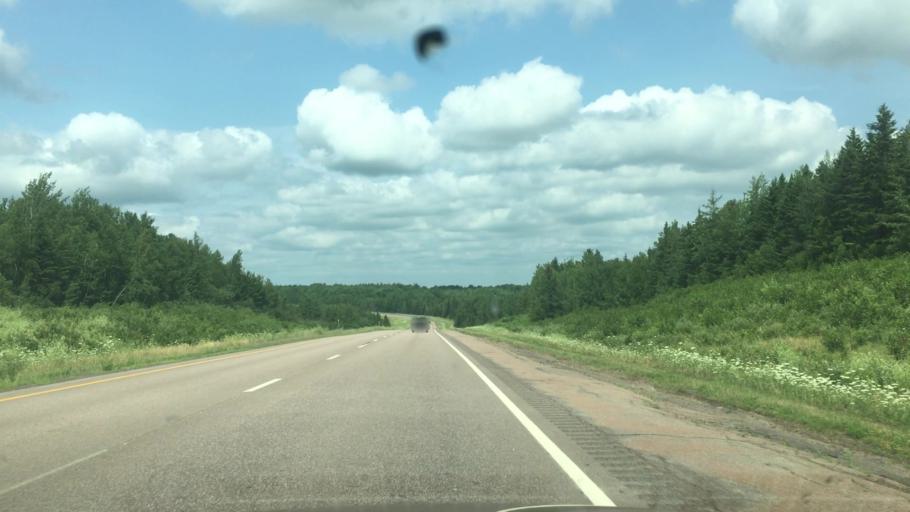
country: CA
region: New Brunswick
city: Dieppe
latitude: 46.0874
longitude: -64.5953
